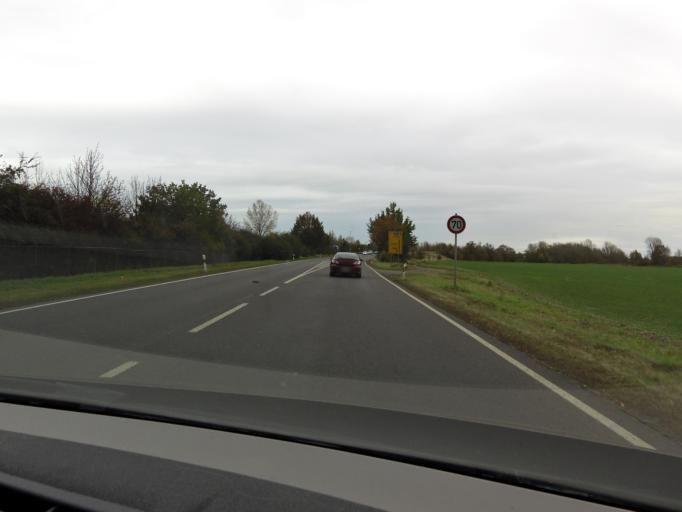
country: DE
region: Saxony
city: Zwenkau
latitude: 51.2114
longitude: 12.3421
